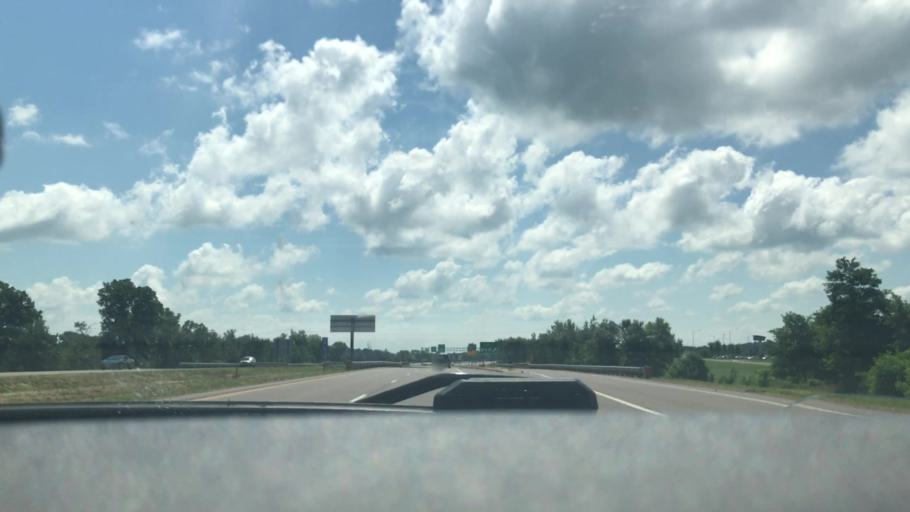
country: US
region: Wisconsin
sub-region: Eau Claire County
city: Altoona
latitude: 44.7729
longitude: -91.4293
